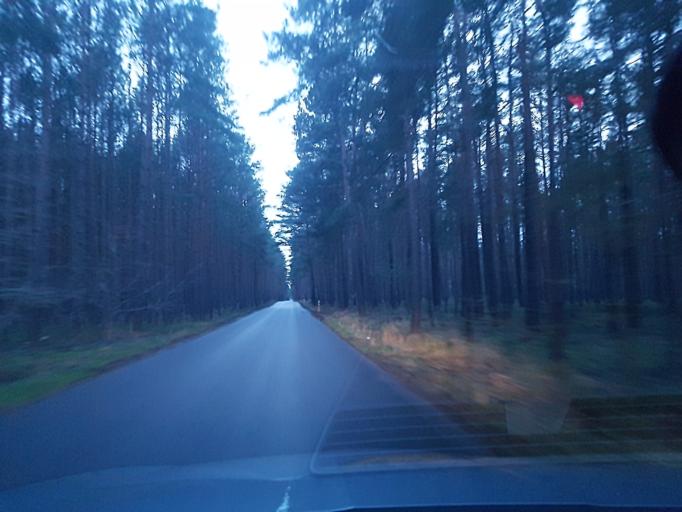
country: DE
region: Brandenburg
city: Ruckersdorf
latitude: 51.5914
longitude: 13.5966
